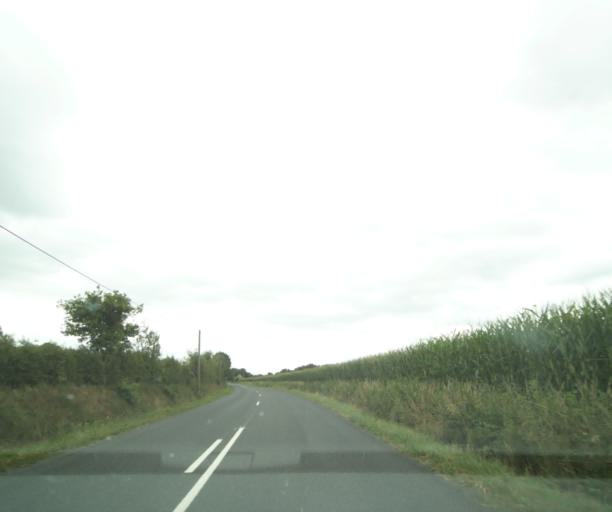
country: FR
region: Pays de la Loire
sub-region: Departement de la Sarthe
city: Precigne
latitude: 47.7574
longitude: -0.3098
